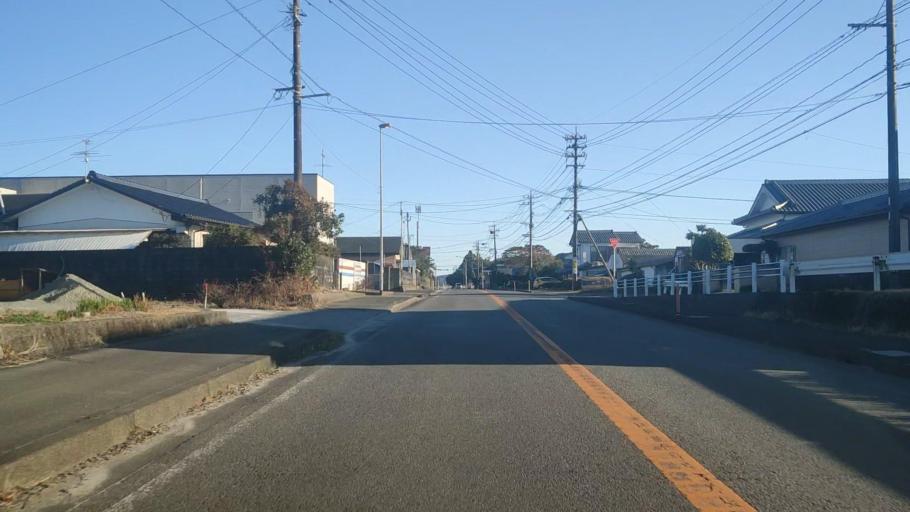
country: JP
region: Miyazaki
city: Takanabe
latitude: 32.3140
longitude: 131.5888
